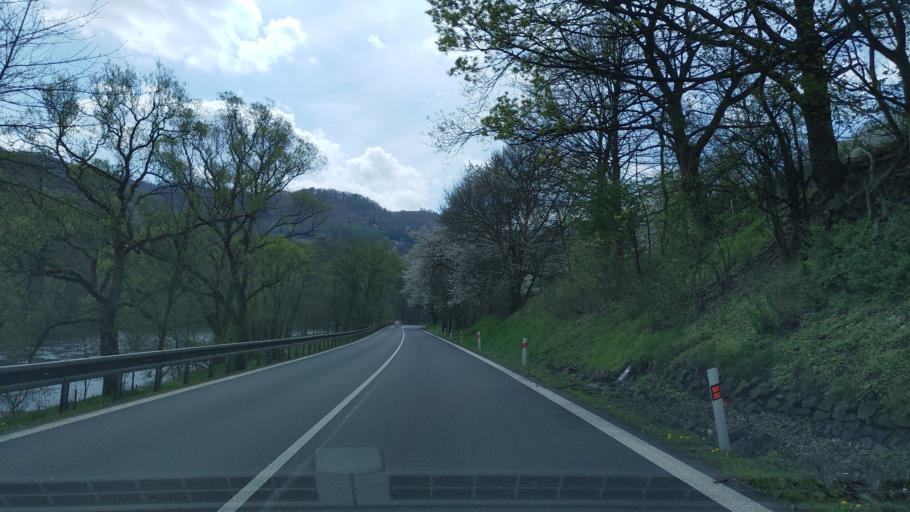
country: CZ
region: Ustecky
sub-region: Okres Chomutov
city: Perstejn
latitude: 50.3553
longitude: 13.0742
